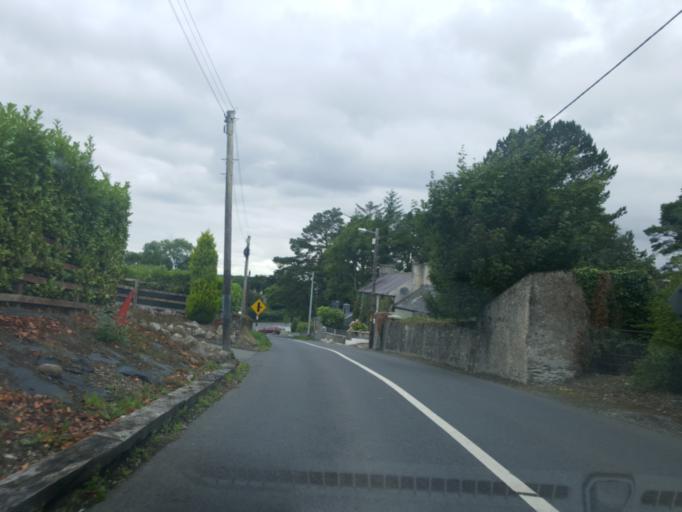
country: IE
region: Leinster
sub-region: Wicklow
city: Valleymount
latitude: 53.1319
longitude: -6.6079
